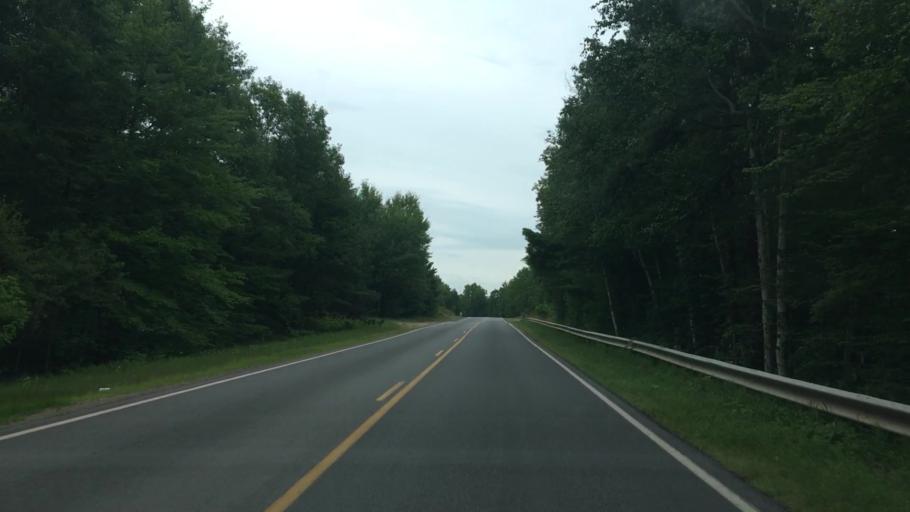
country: US
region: New York
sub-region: Essex County
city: Keeseville
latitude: 44.4773
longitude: -73.5955
